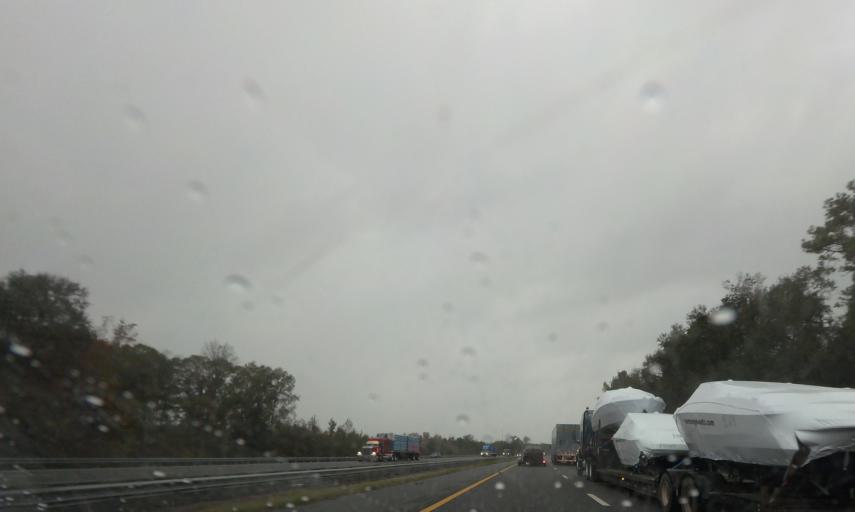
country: US
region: Florida
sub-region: Hamilton County
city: Jasper
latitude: 30.5002
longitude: -83.0420
